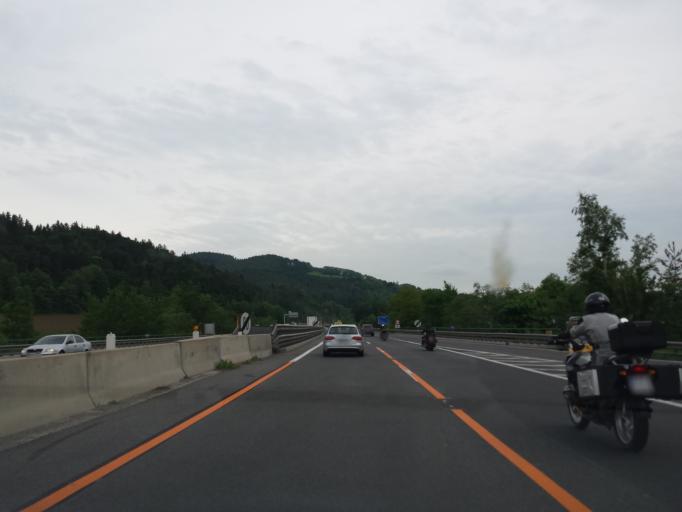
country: AT
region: Lower Austria
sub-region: Politischer Bezirk Neunkirchen
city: Grimmenstein
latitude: 47.6302
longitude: 16.1294
